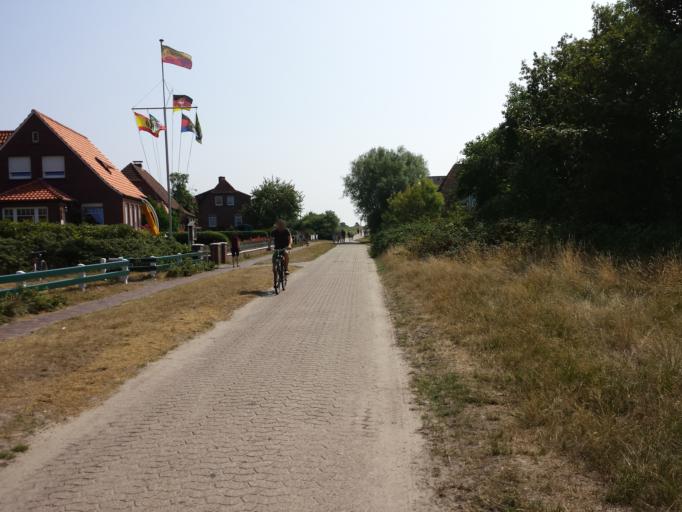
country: DE
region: Lower Saxony
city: Spiekeroog
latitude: 53.7701
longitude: 7.7017
